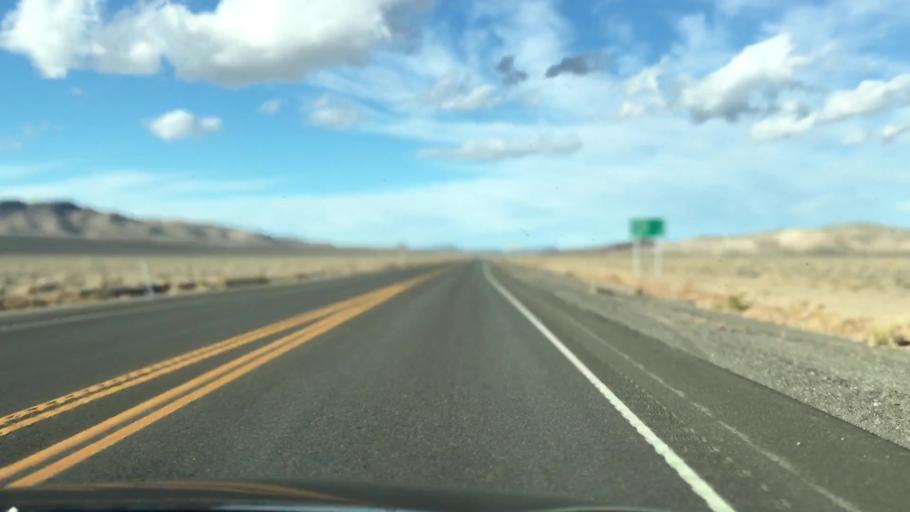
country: US
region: Nevada
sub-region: Esmeralda County
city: Goldfield
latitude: 37.5047
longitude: -117.1855
